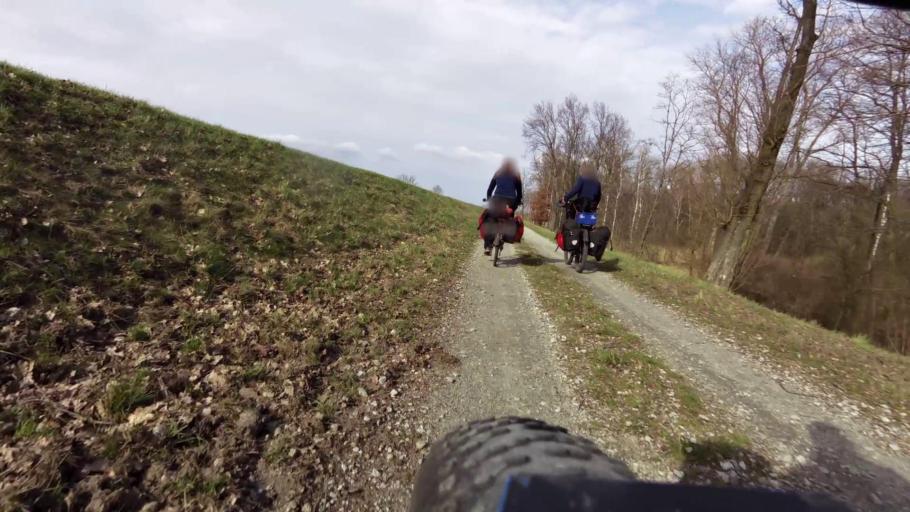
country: DE
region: Brandenburg
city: Reitwein
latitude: 52.5341
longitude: 14.6123
